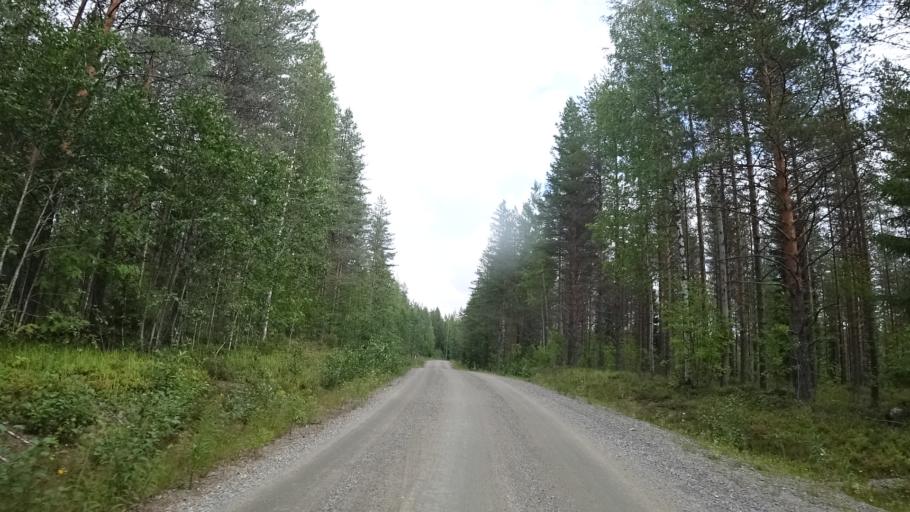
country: FI
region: North Karelia
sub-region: Joensuu
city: Ilomantsi
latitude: 62.9205
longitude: 31.3443
